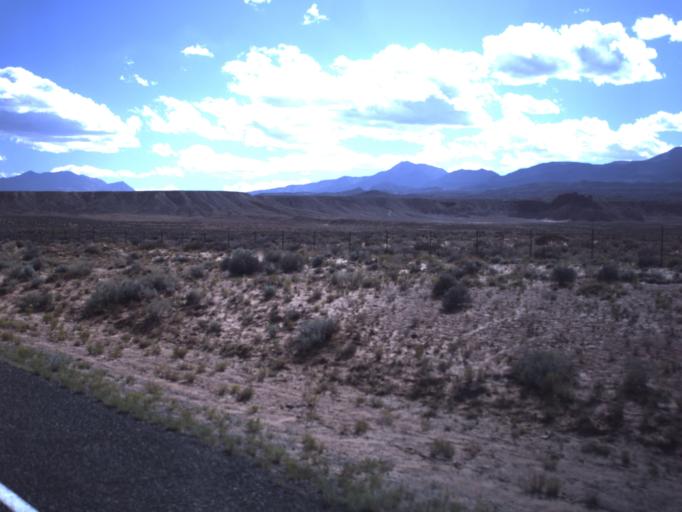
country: US
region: Utah
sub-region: Wayne County
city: Loa
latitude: 38.1617
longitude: -110.6223
